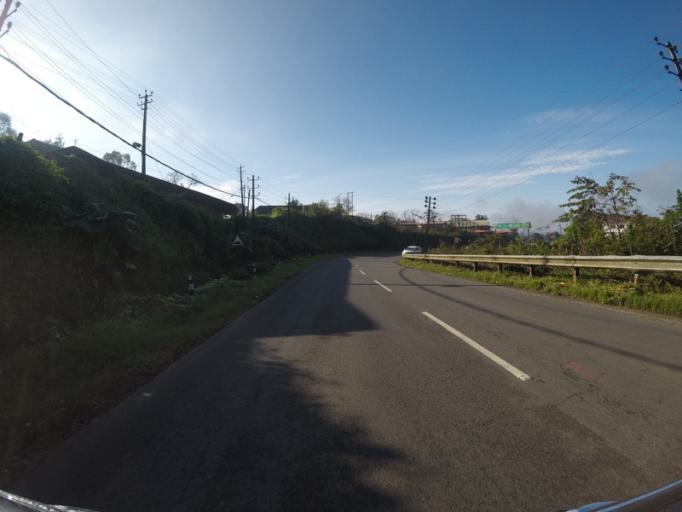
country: IN
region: Karnataka
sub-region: Kodagu
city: Madikeri
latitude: 12.4182
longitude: 75.7499
